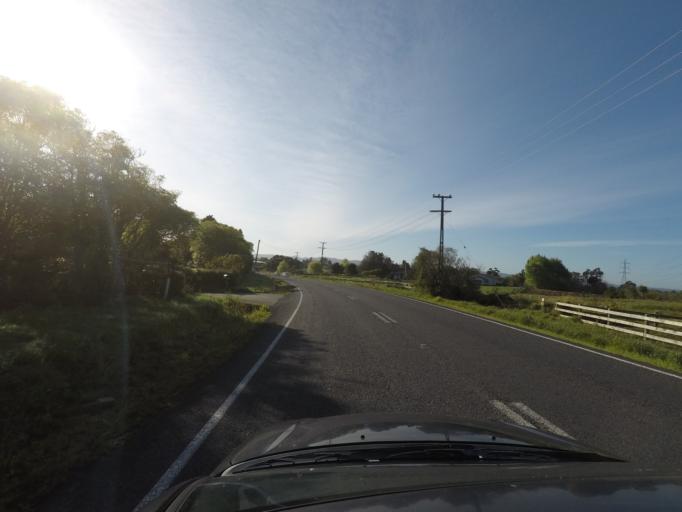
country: NZ
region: Auckland
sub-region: Auckland
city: Takanini
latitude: -37.0168
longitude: 174.9224
